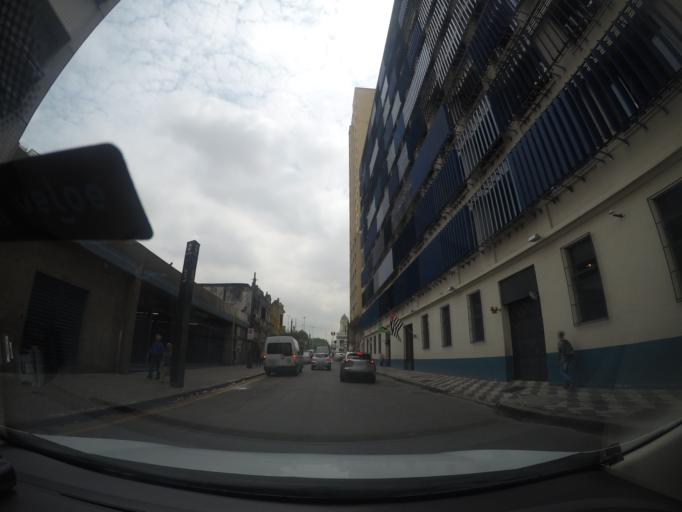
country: BR
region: Sao Paulo
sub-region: Sao Paulo
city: Sao Paulo
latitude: -23.5368
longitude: -46.6330
